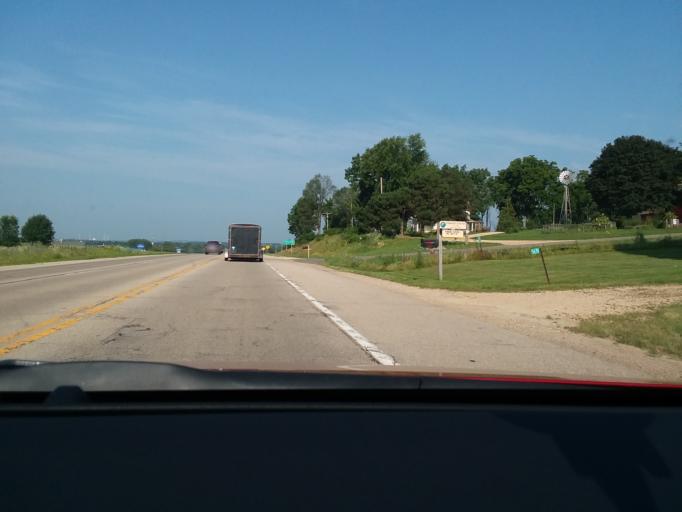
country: US
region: Wisconsin
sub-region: Dane County
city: Waunakee
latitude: 43.1920
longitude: -89.4313
